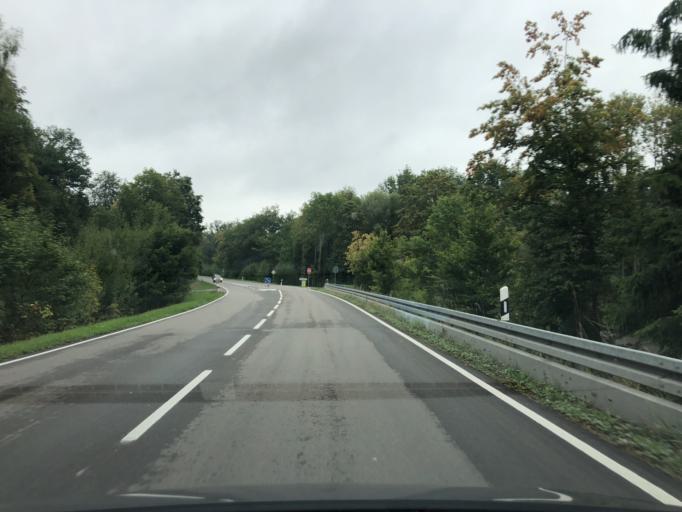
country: DE
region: Baden-Wuerttemberg
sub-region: Regierungsbezirk Stuttgart
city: Gerlingen
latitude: 48.7477
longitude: 9.0582
